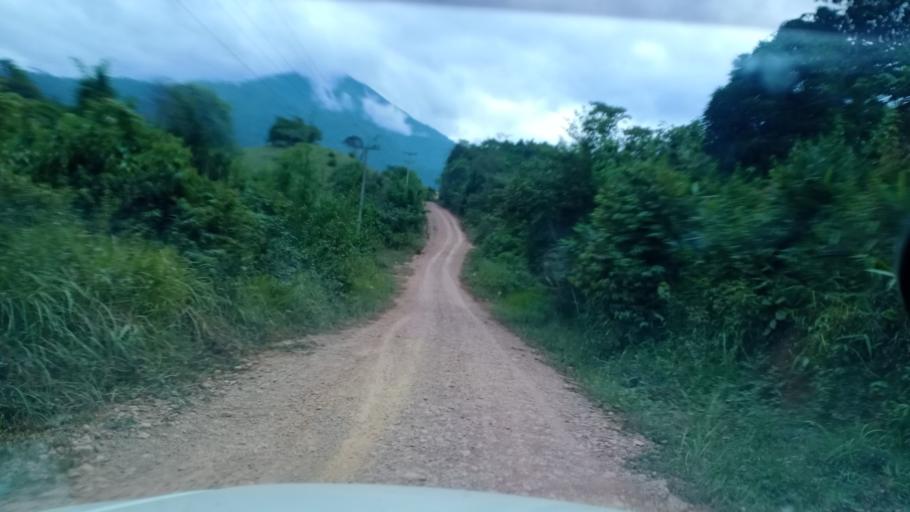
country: TH
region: Changwat Bueng Kan
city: Pak Khat
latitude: 18.7179
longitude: 103.2233
